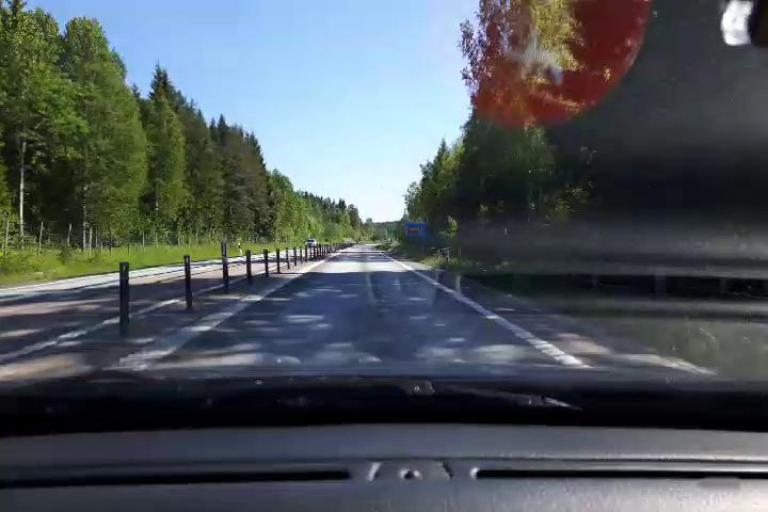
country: SE
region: Gaevleborg
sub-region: Soderhamns Kommun
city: Soderhamn
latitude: 61.2851
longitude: 17.0252
